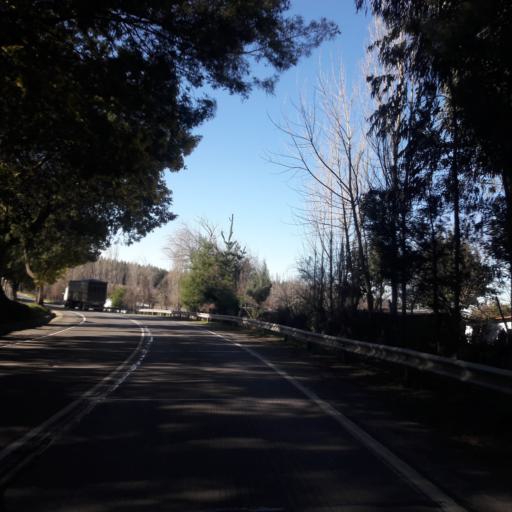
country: CL
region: Araucania
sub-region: Provincia de Malleco
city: Angol
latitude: -37.7417
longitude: -72.6116
